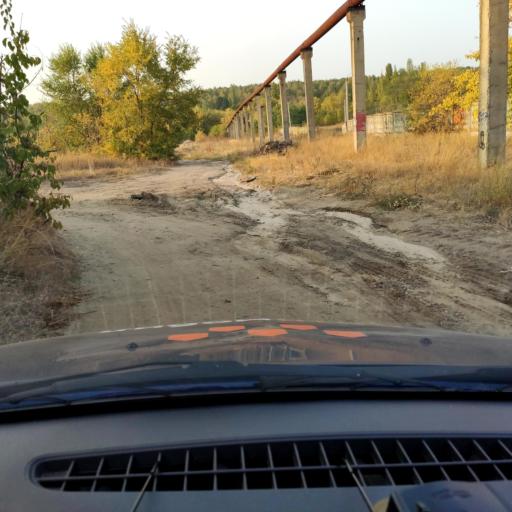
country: RU
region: Voronezj
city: Pridonskoy
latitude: 51.6647
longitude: 39.1127
